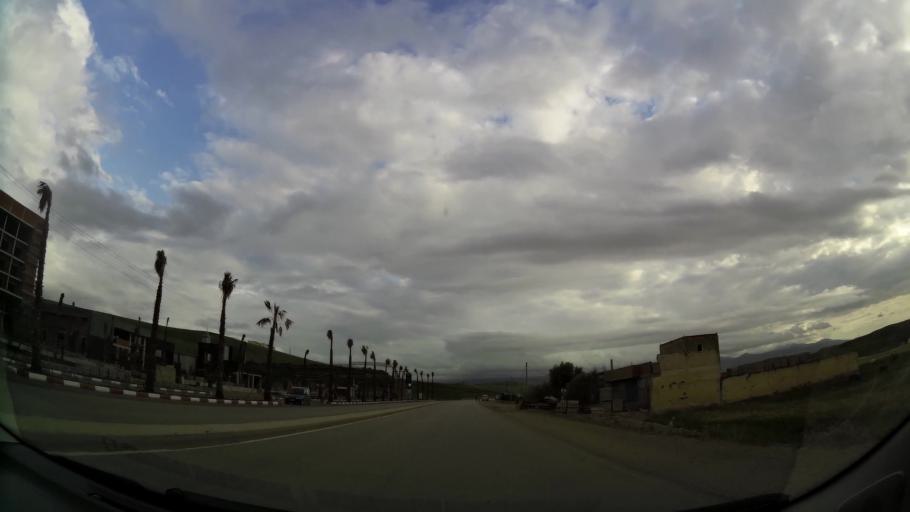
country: MA
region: Taza-Al Hoceima-Taounate
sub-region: Taza
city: Taza
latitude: 34.2677
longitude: -3.9570
